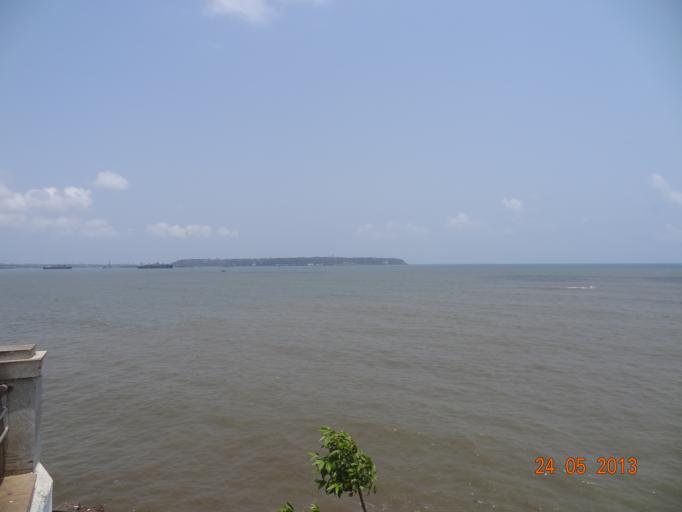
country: IN
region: Goa
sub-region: North Goa
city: Taleigao
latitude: 15.4506
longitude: 73.8030
